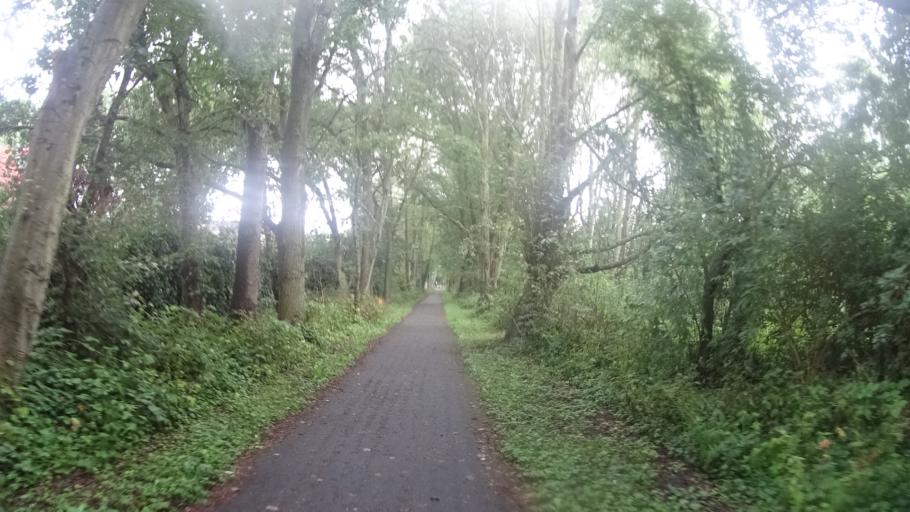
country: DE
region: Lower Saxony
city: Leer
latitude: 53.2444
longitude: 7.4894
